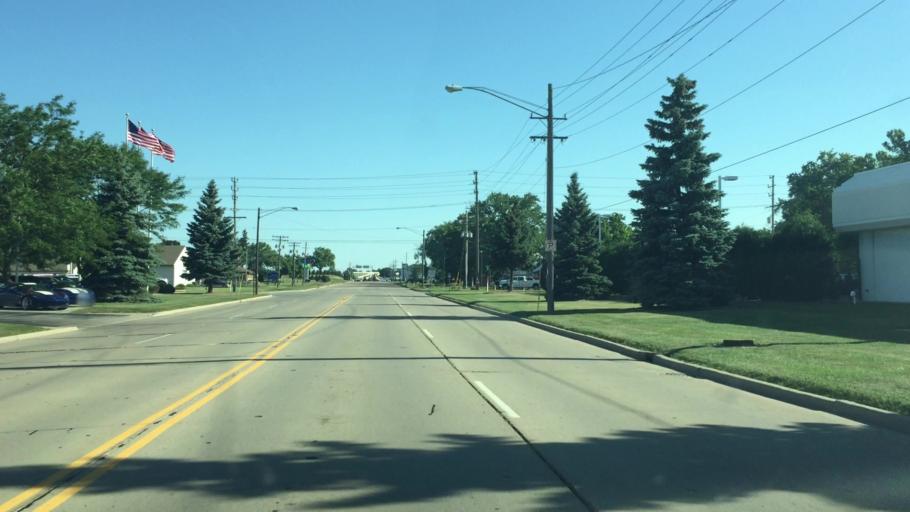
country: US
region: Wisconsin
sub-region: Winnebago County
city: Neenah
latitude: 44.1917
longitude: -88.4851
